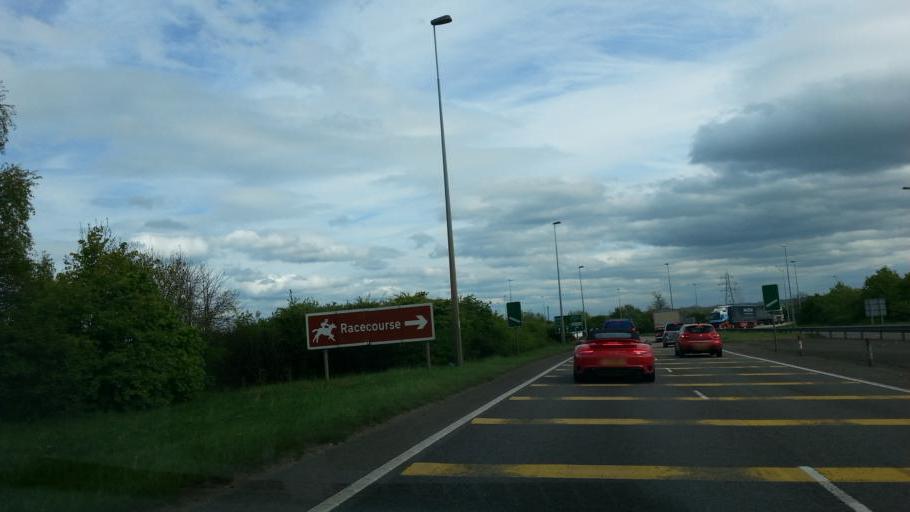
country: GB
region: England
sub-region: Staffordshire
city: Uttoxeter
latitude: 52.9084
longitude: -1.8551
